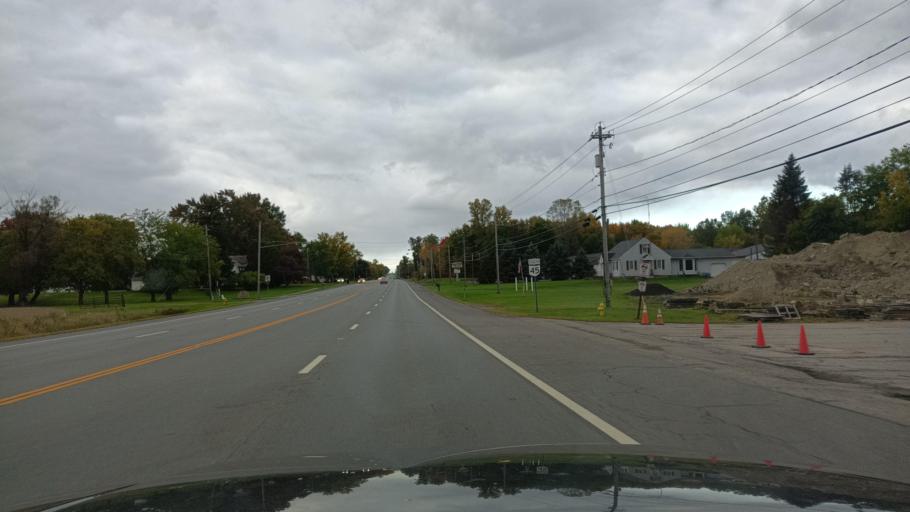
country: US
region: Ohio
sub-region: Trumbull County
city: Lordstown
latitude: 41.1754
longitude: -80.8575
